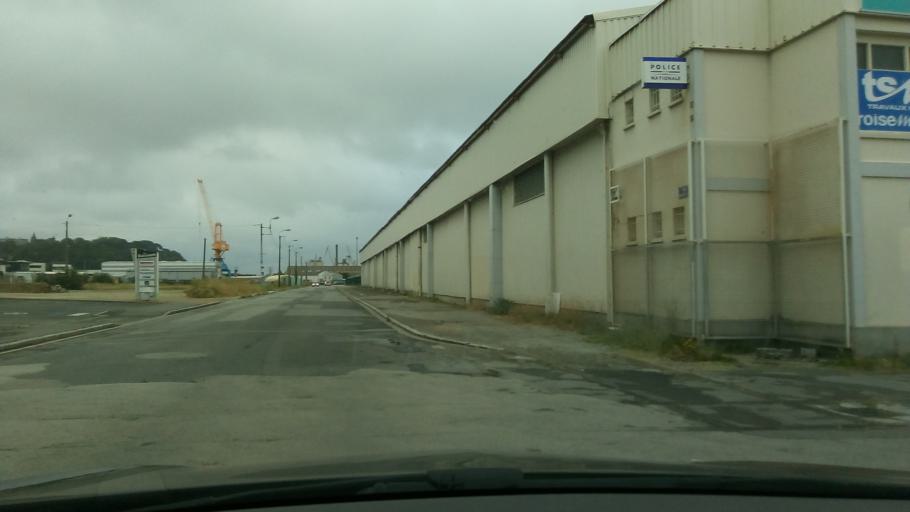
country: FR
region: Brittany
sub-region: Departement du Finistere
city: Brest
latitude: 48.3831
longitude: -4.4826
